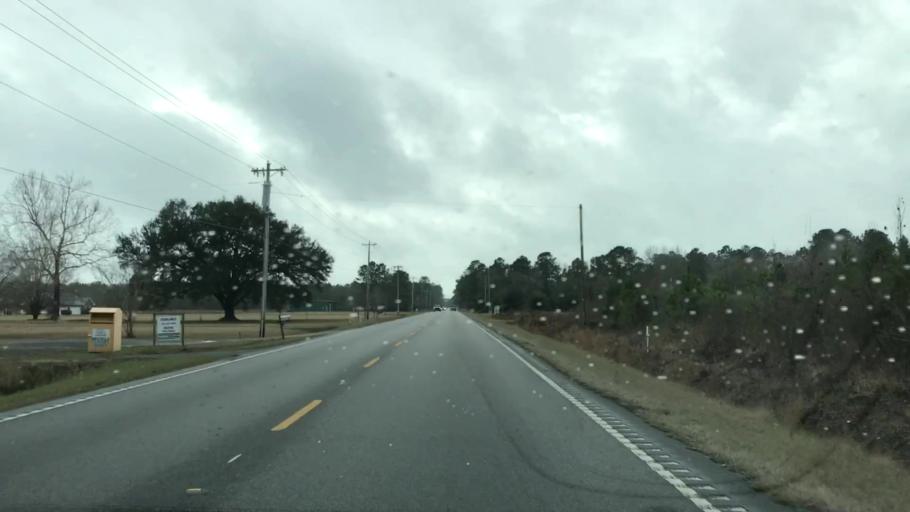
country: US
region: South Carolina
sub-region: Horry County
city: Socastee
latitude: 33.7365
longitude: -79.0811
